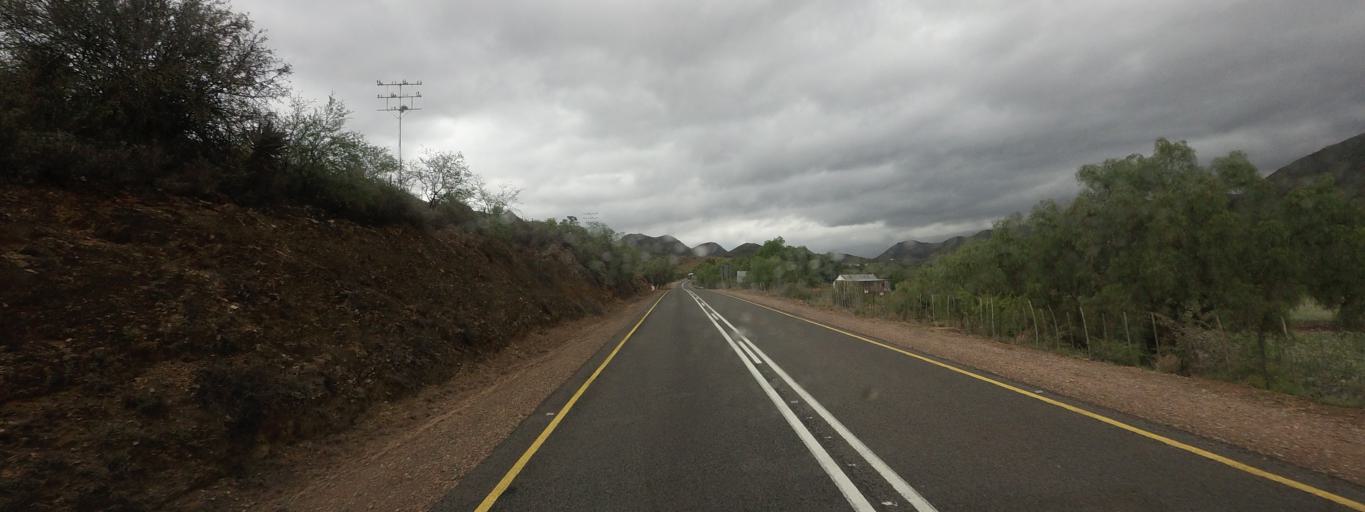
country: ZA
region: Western Cape
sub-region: Eden District Municipality
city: Oudtshoorn
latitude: -33.4070
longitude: 22.2280
